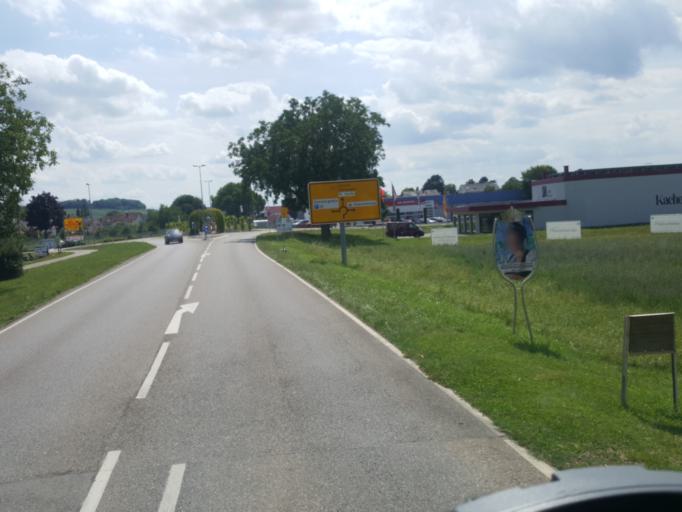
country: DE
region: Baden-Wuerttemberg
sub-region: Freiburg Region
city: Auggen
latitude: 47.7925
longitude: 7.5928
